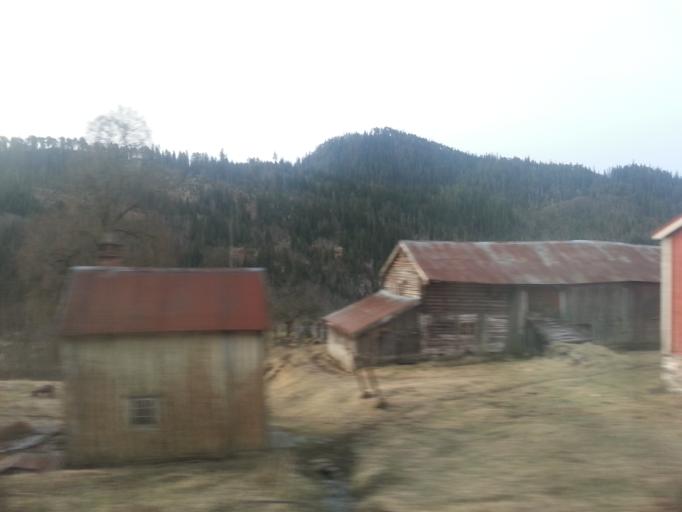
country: NO
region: Sor-Trondelag
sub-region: Midtre Gauldal
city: Storen
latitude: 63.0252
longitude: 10.2500
